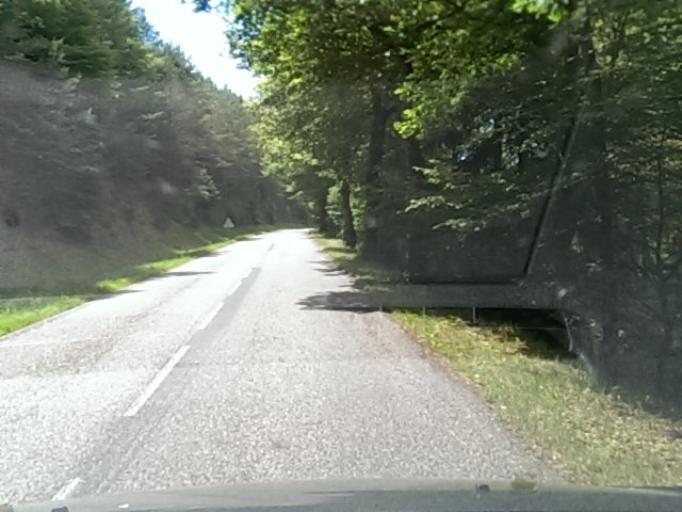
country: FR
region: Lorraine
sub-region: Departement de la Moselle
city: Bitche
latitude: 48.9836
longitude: 7.4830
